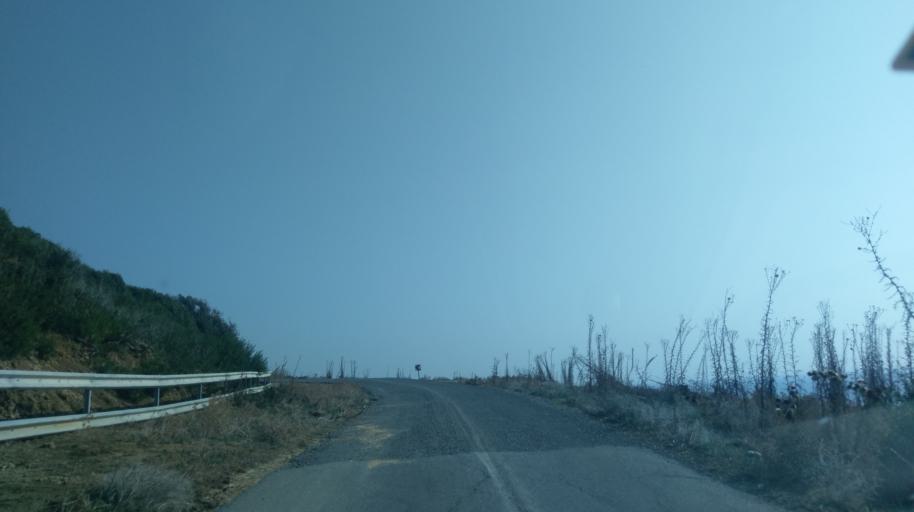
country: CY
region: Ammochostos
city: Rizokarpaso
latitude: 35.6447
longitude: 34.5559
